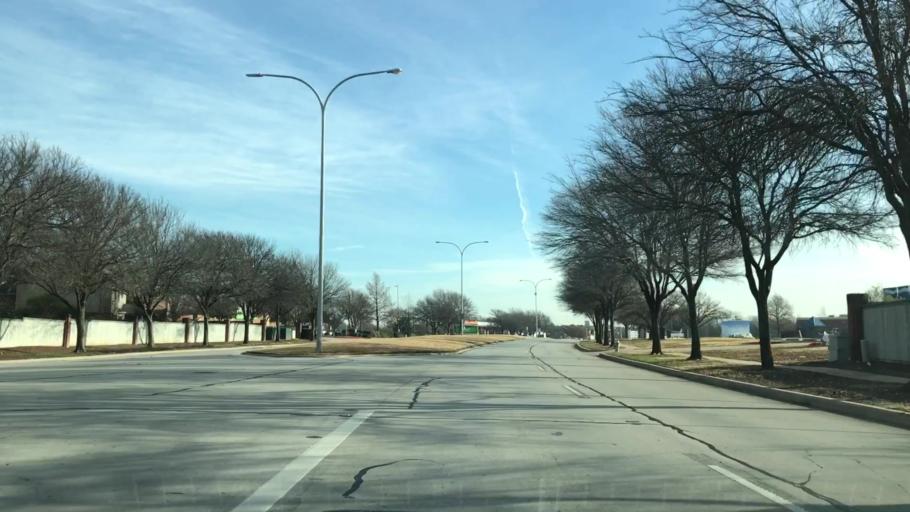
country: US
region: Texas
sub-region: Tarrant County
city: Watauga
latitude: 32.8736
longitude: -97.2722
